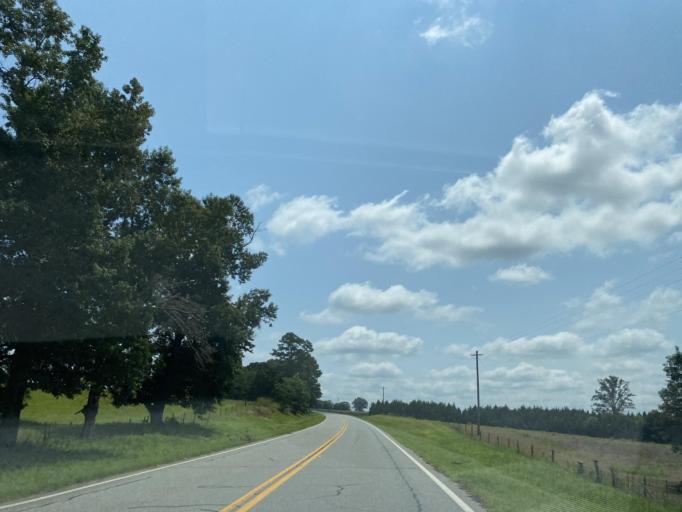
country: US
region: Georgia
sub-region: Wilcox County
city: Abbeville
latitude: 32.0026
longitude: -83.1502
